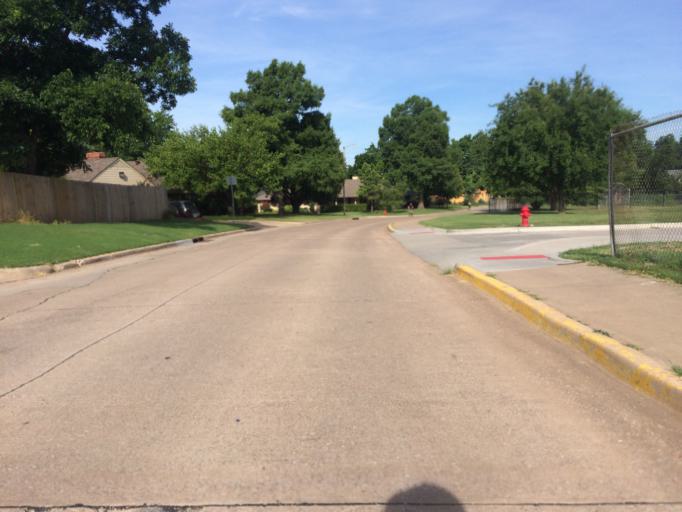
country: US
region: Oklahoma
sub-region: Cleveland County
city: Norman
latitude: 35.2242
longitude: -97.4692
